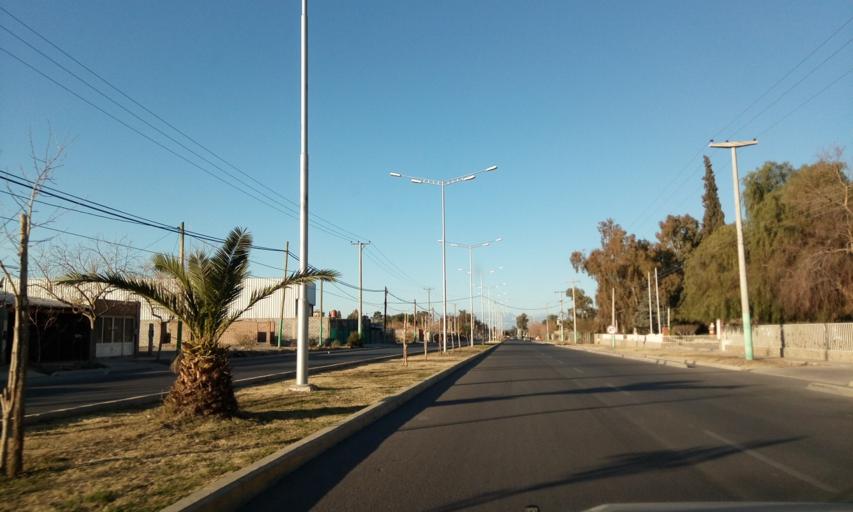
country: AR
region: San Juan
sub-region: Departamento de Rivadavia
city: Rivadavia
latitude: -31.5241
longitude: -68.6236
